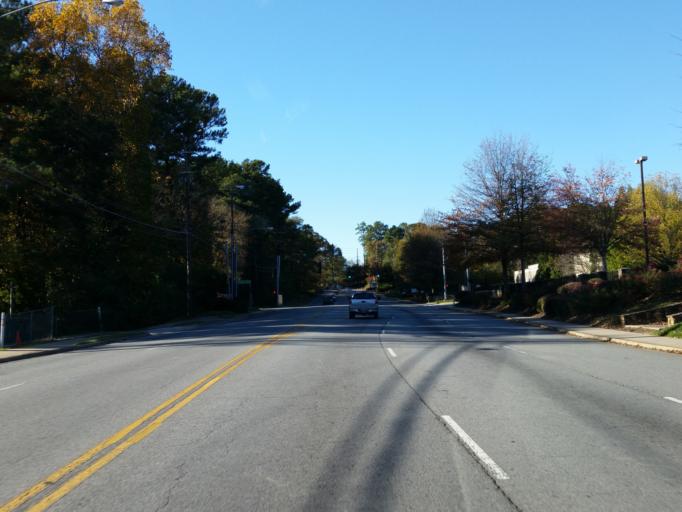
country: US
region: Georgia
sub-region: Cobb County
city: Smyrna
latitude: 33.9297
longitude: -84.4958
